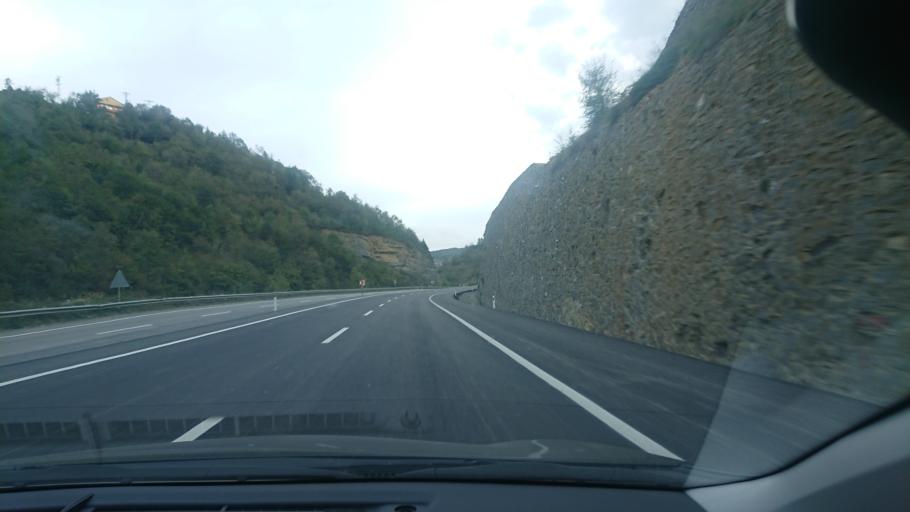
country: TR
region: Zonguldak
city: Beycuma
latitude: 41.3910
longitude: 31.9360
